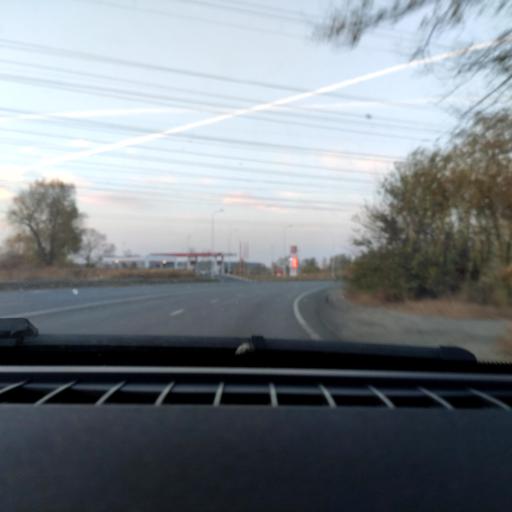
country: RU
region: Voronezj
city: Maslovka
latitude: 51.6286
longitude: 39.2864
